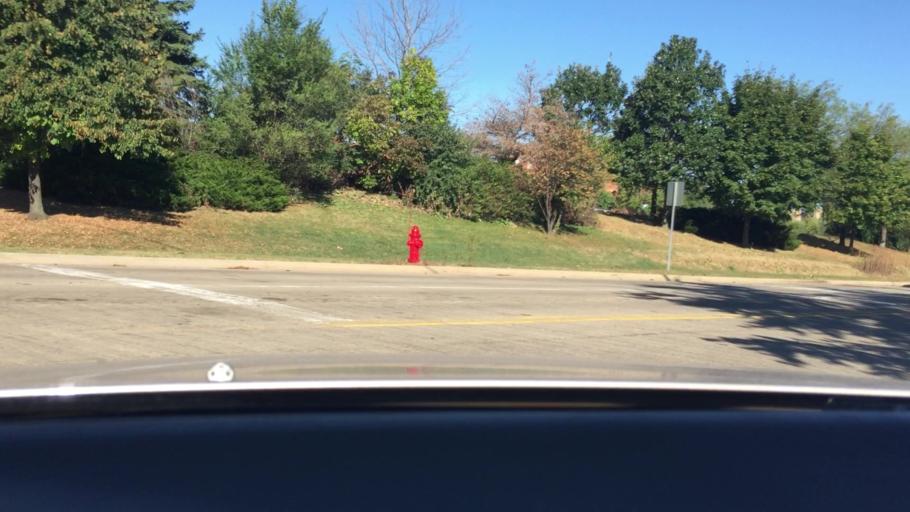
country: US
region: Illinois
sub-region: Lake County
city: Forest Lake
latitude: 42.1975
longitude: -88.0677
